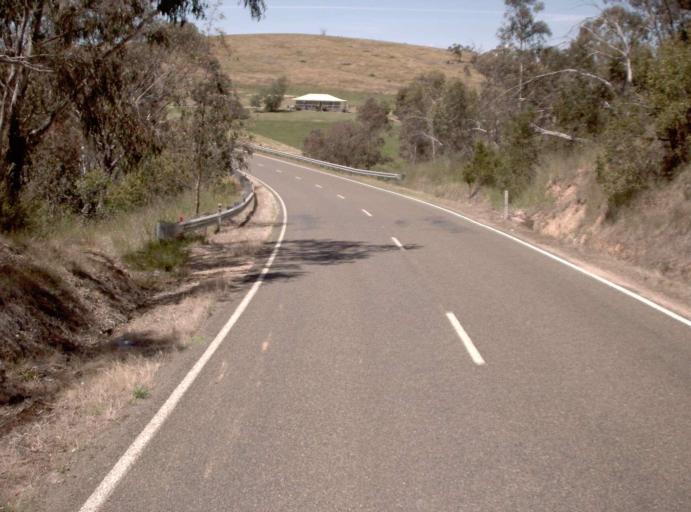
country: AU
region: Victoria
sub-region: Alpine
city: Mount Beauty
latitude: -37.1052
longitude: 147.6025
